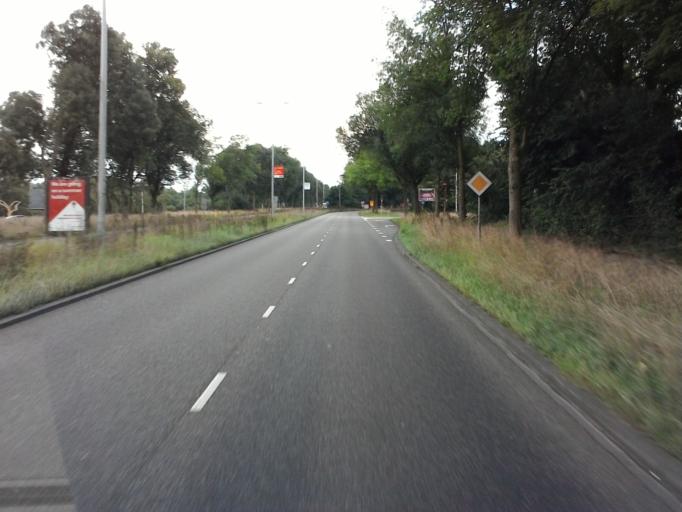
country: NL
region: Utrecht
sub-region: Gemeente Utrecht
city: Utrecht
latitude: 52.1242
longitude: 5.1134
